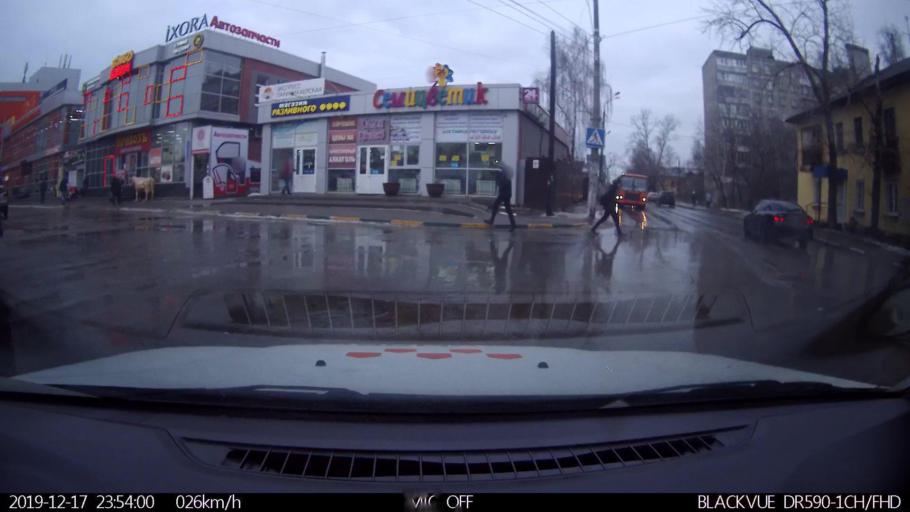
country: RU
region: Nizjnij Novgorod
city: Gorbatovka
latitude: 56.3649
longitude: 43.8172
